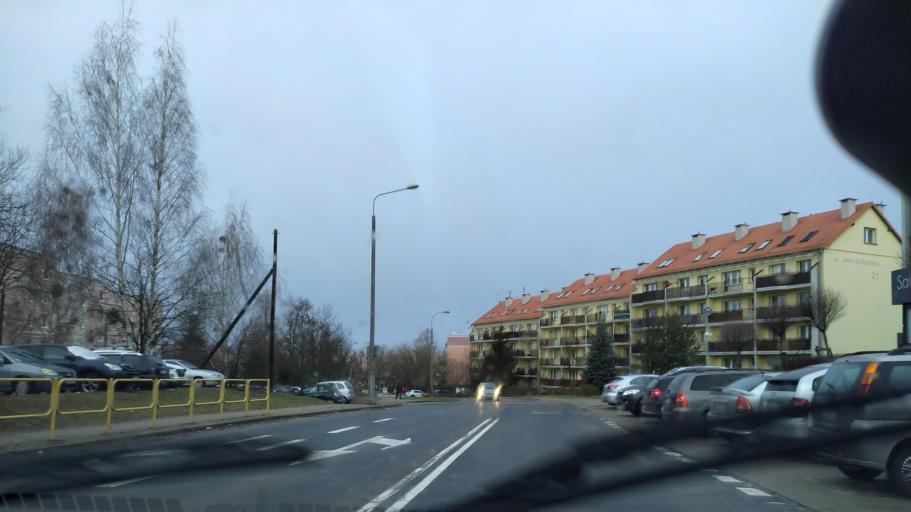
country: PL
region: Warmian-Masurian Voivodeship
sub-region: Powiat olsztynski
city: Olsztyn
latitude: 53.7419
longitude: 20.5017
